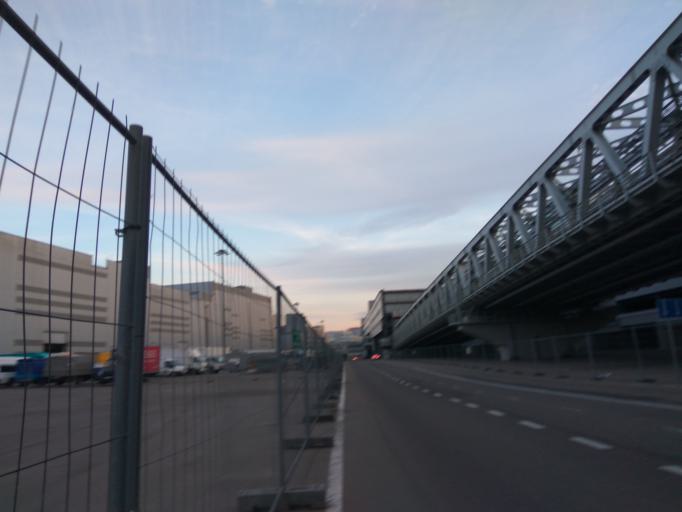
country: RU
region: Moscow
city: Strogino
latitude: 55.8286
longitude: 37.3855
